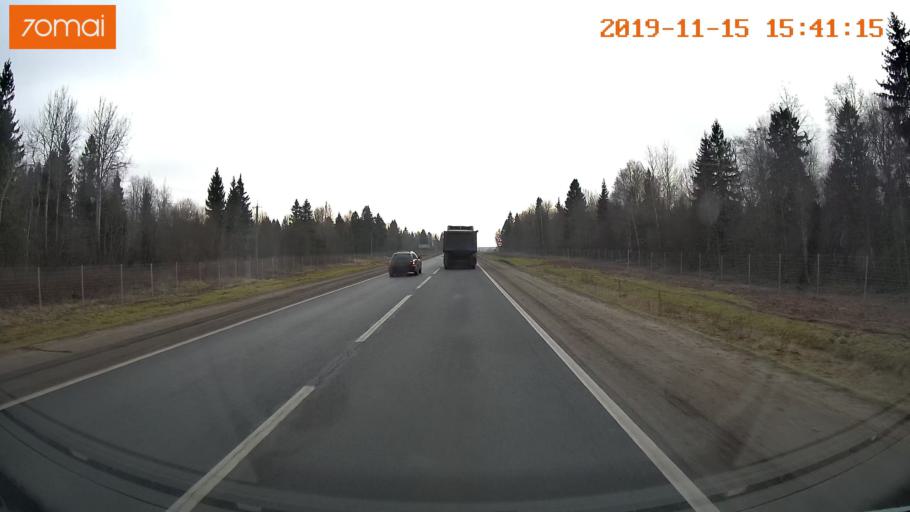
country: RU
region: Jaroslavl
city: Danilov
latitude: 58.0027
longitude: 40.0496
